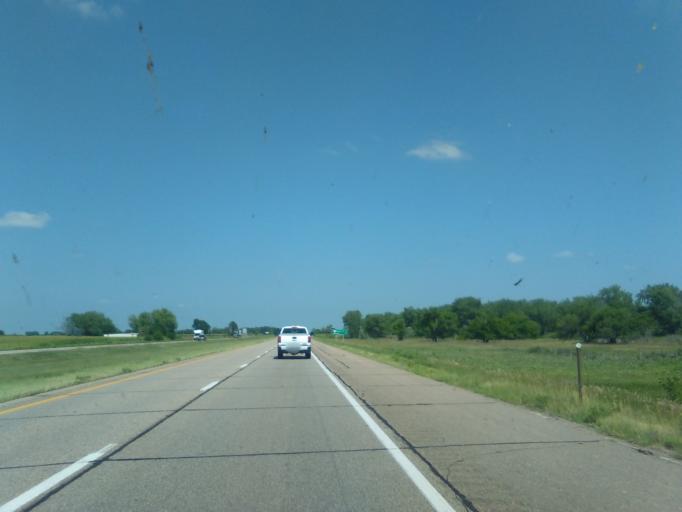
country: US
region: Nebraska
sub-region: Phelps County
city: Holdrege
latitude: 40.6905
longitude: -99.3656
